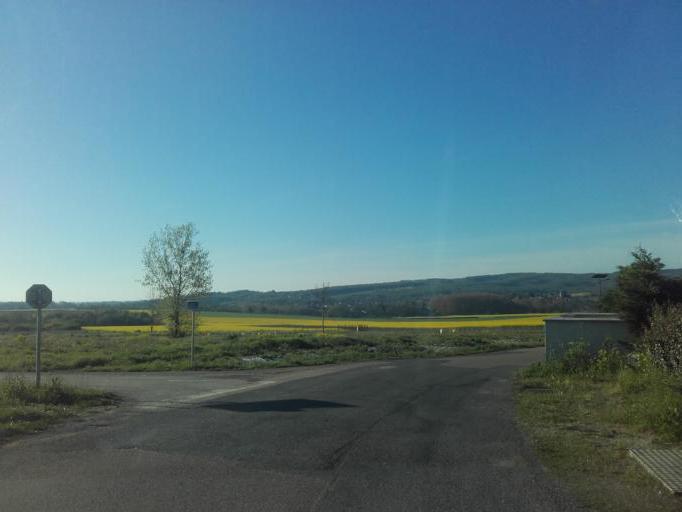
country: FR
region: Bourgogne
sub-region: Departement de Saone-et-Loire
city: Mellecey
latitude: 46.8233
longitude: 4.7288
